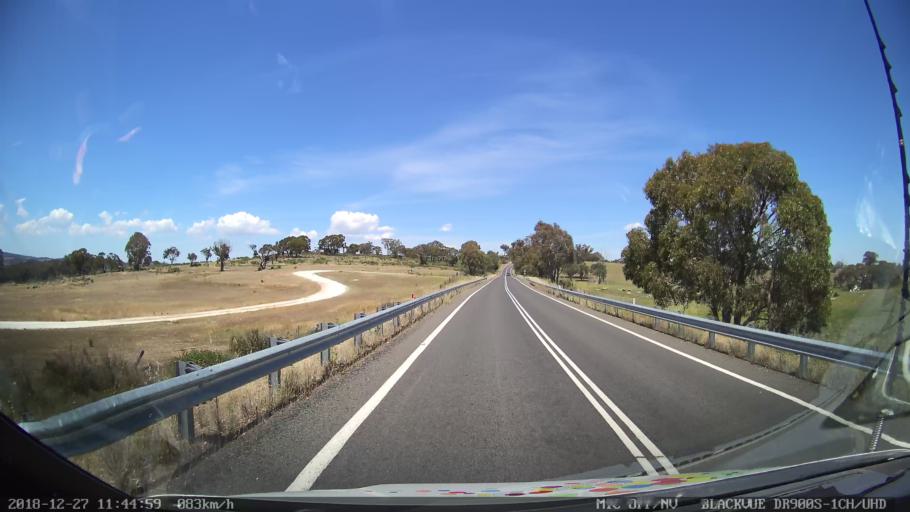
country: AU
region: New South Wales
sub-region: Bathurst Regional
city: Perthville
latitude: -33.5786
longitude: 149.4752
